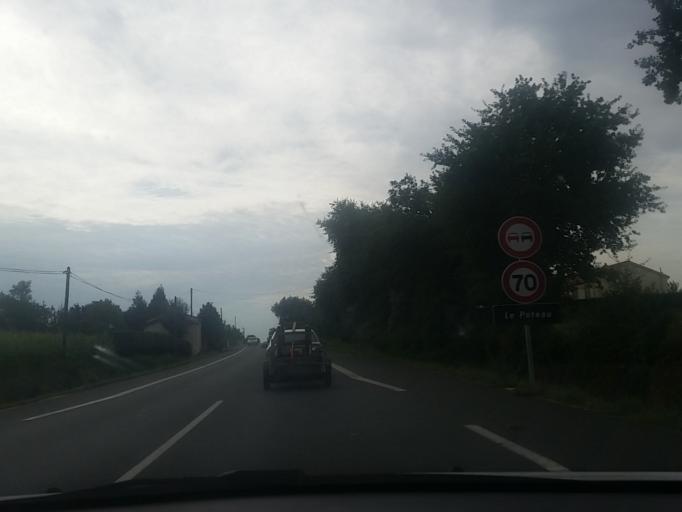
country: FR
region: Pays de la Loire
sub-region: Departement de la Vendee
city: Chavagnes-en-Paillers
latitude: 46.8922
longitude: -1.2233
